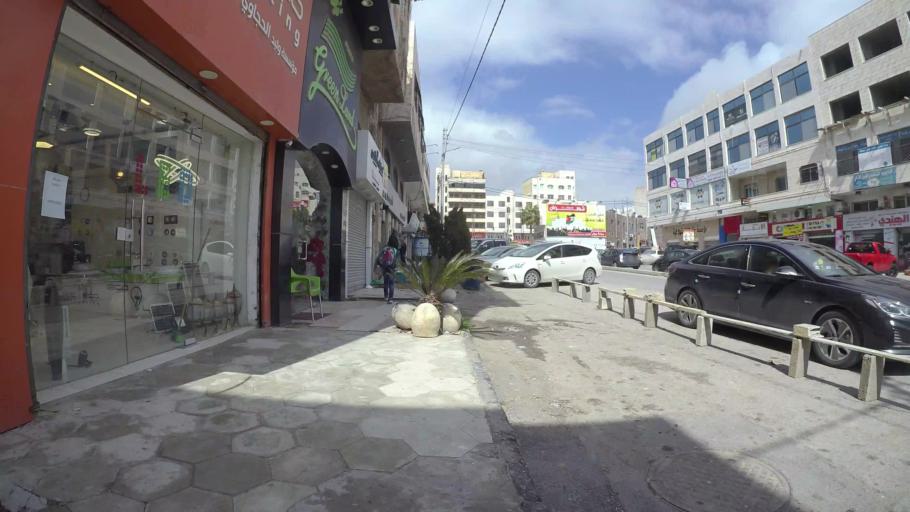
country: JO
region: Amman
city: Al Jubayhah
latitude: 31.9959
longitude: 35.8482
